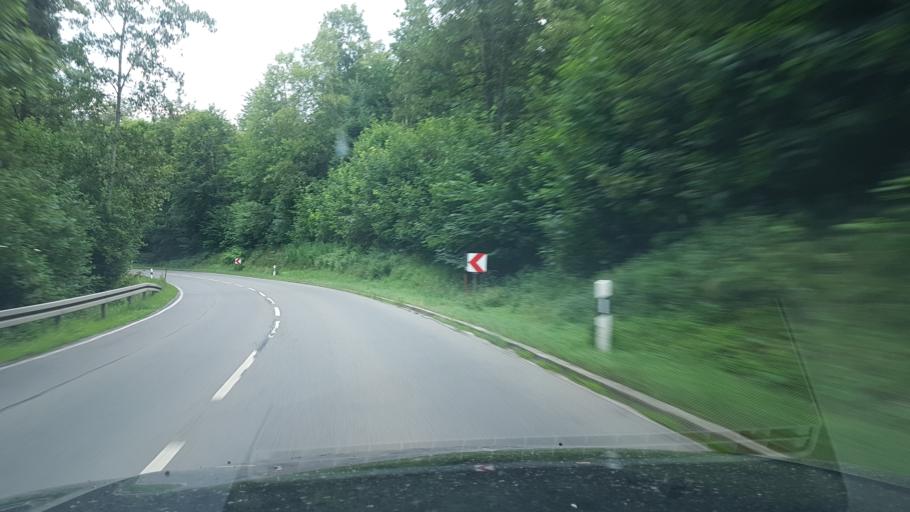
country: DE
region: Baden-Wuerttemberg
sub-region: Freiburg Region
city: Donaueschingen
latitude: 47.9576
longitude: 8.4712
